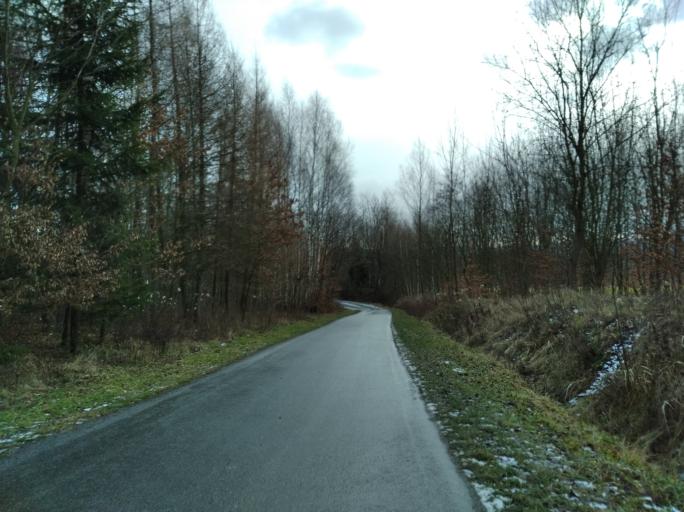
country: PL
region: Subcarpathian Voivodeship
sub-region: Powiat strzyzowski
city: Wysoka Strzyzowska
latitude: 49.8923
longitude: 21.7266
